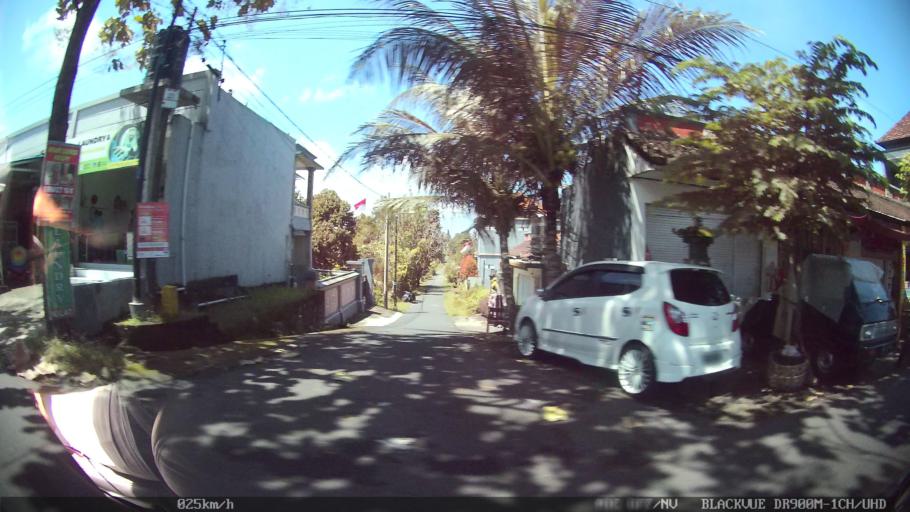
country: ID
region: Bali
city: Banjar Kelodan
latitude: -8.5378
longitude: 115.3348
